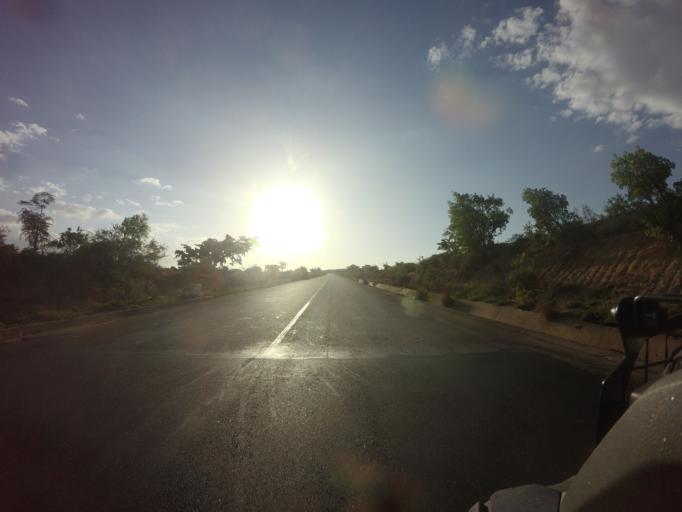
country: AO
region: Huila
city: Lubango
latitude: -14.7865
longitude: 13.7182
